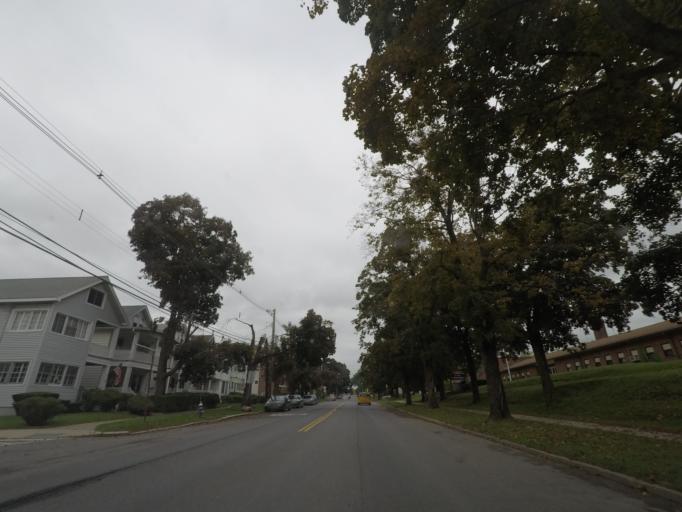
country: US
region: New York
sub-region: Albany County
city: West Albany
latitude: 42.6679
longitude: -73.7854
